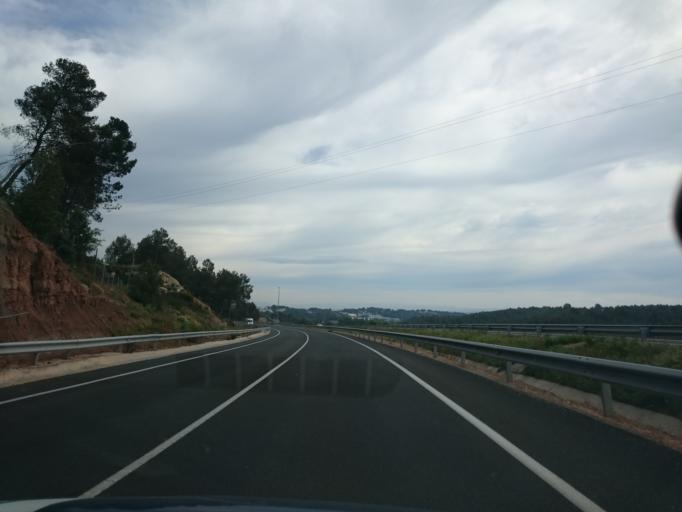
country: ES
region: Catalonia
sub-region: Provincia de Barcelona
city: Sant Salvador de Guardiola
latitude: 41.6910
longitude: 1.7783
